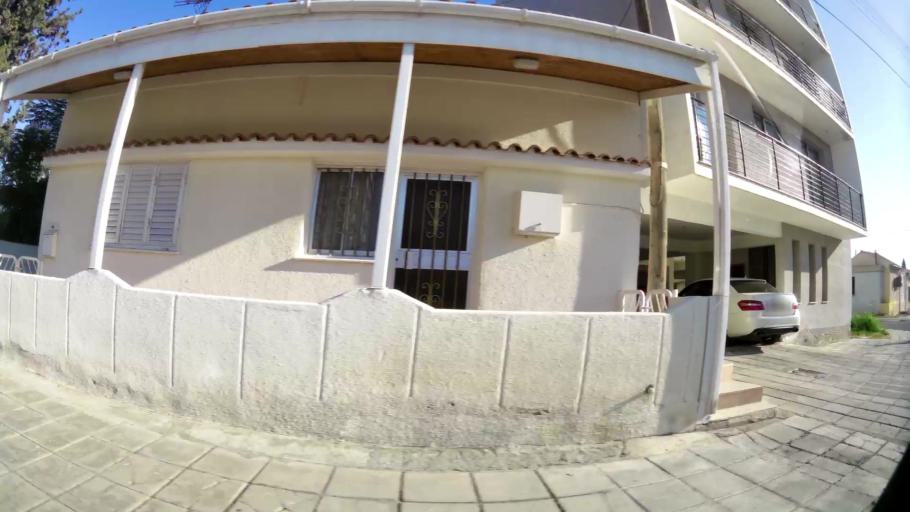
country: CY
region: Larnaka
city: Larnaca
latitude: 34.9226
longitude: 33.6208
